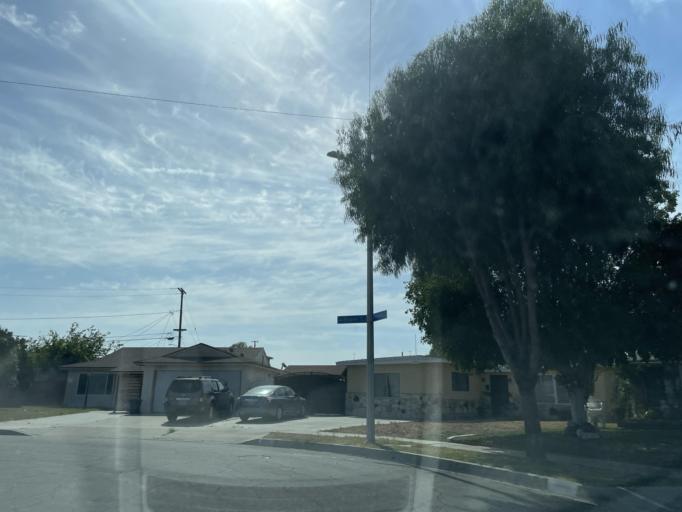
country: US
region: California
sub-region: Los Angeles County
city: Norwalk
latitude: 33.9111
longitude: -118.0603
